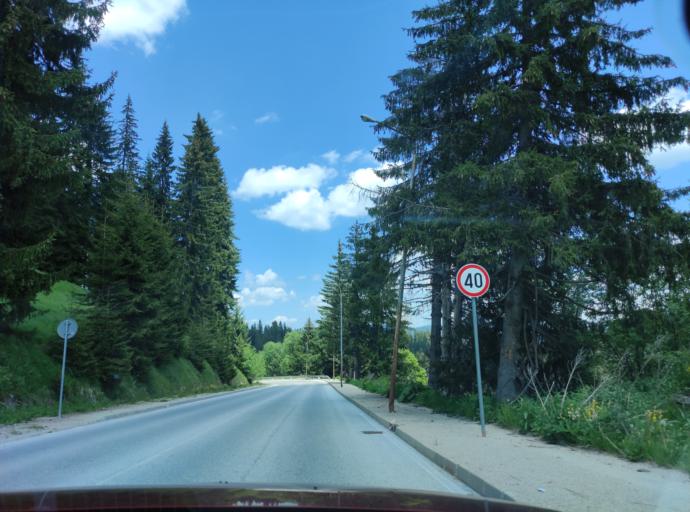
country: BG
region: Smolyan
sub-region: Obshtina Smolyan
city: Smolyan
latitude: 41.6479
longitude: 24.6980
